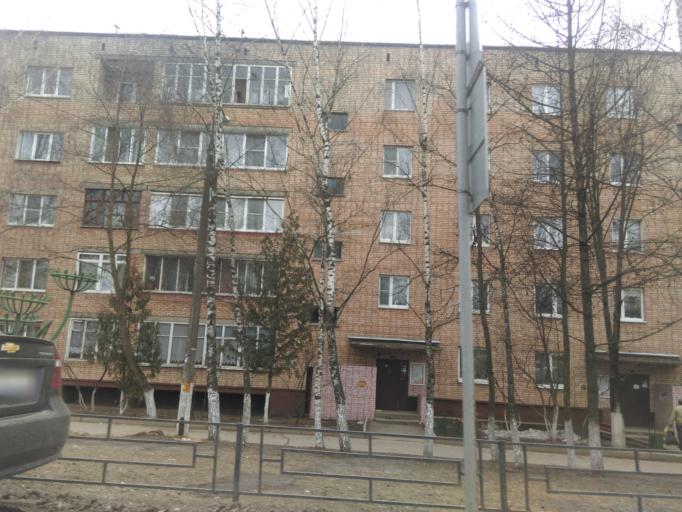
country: RU
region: Moskovskaya
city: Tuchkovo
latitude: 55.6011
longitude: 36.4619
